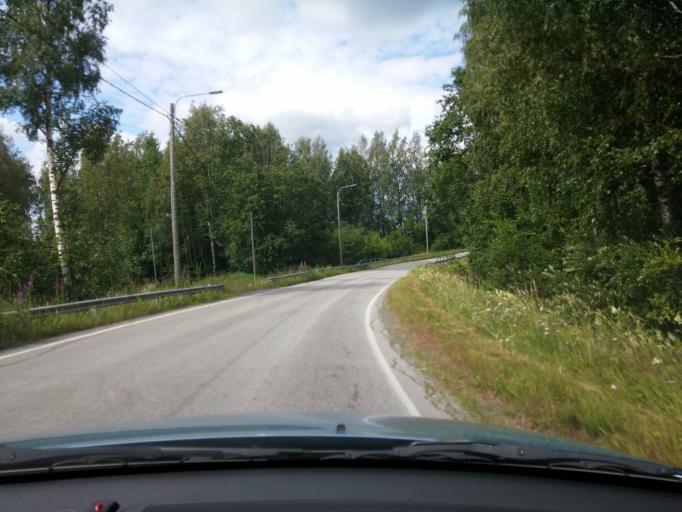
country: FI
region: Central Finland
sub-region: Saarijaervi-Viitasaari
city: Saarijaervi
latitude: 62.7357
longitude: 25.1764
